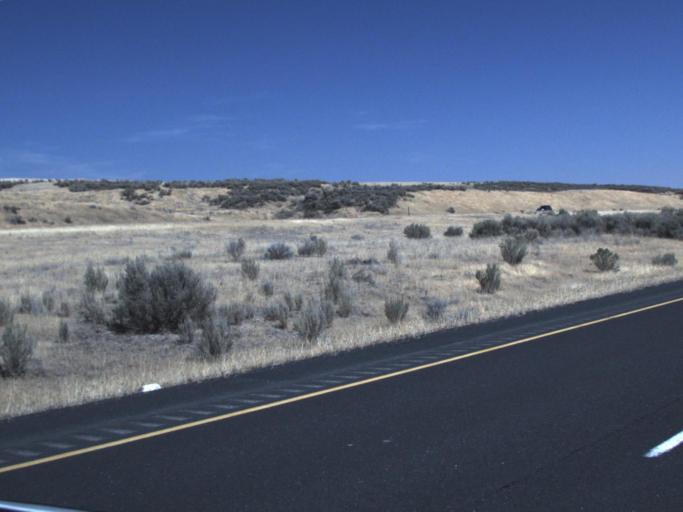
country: US
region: Washington
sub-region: Grant County
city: Warden
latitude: 47.0860
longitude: -118.9367
